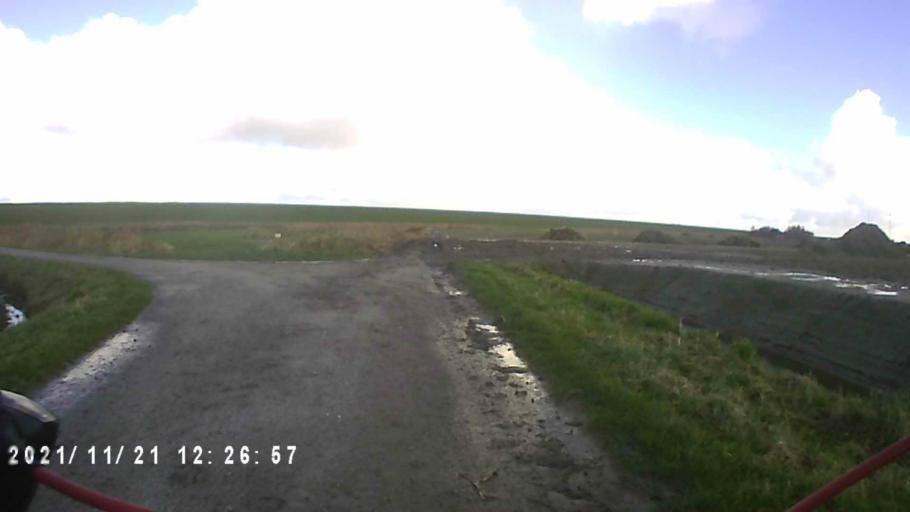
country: NL
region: Friesland
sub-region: Gemeente Dongeradeel
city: Anjum
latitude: 53.4035
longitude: 6.0553
